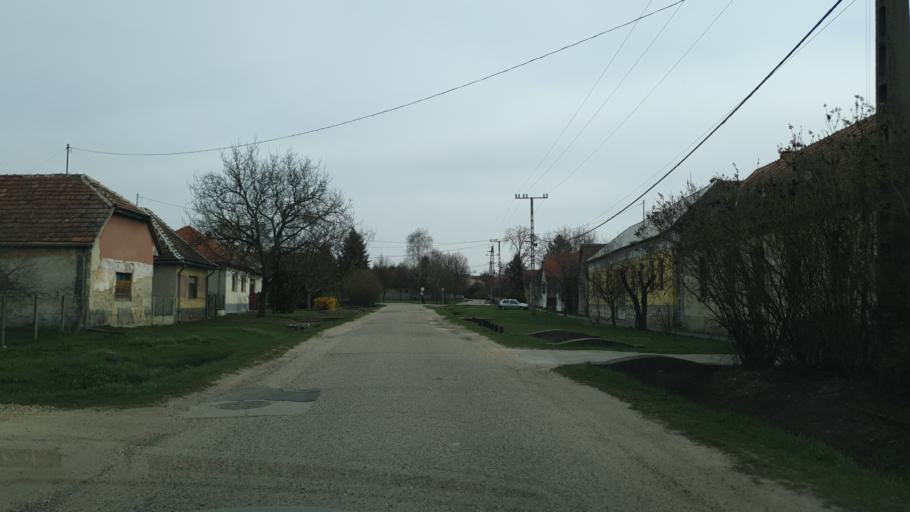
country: HU
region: Fejer
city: Etyek
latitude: 47.4448
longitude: 18.7561
